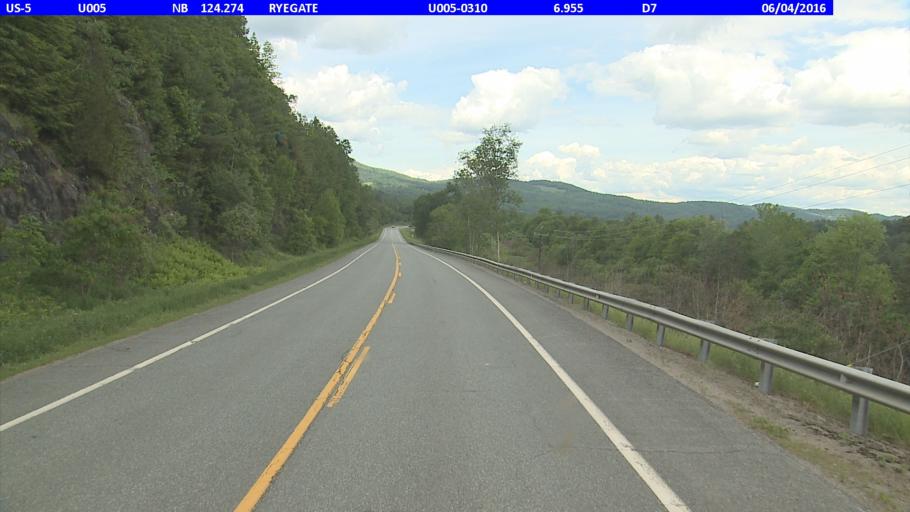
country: US
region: New Hampshire
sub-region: Grafton County
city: Woodsville
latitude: 44.2512
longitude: -72.0573
